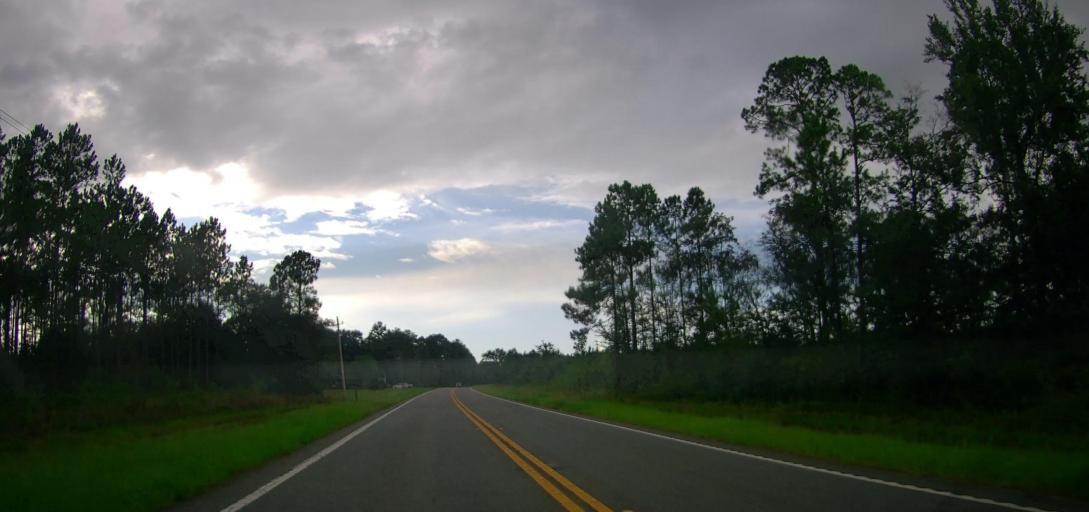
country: US
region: Georgia
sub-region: Ware County
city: Deenwood
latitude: 31.2866
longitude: -82.5491
